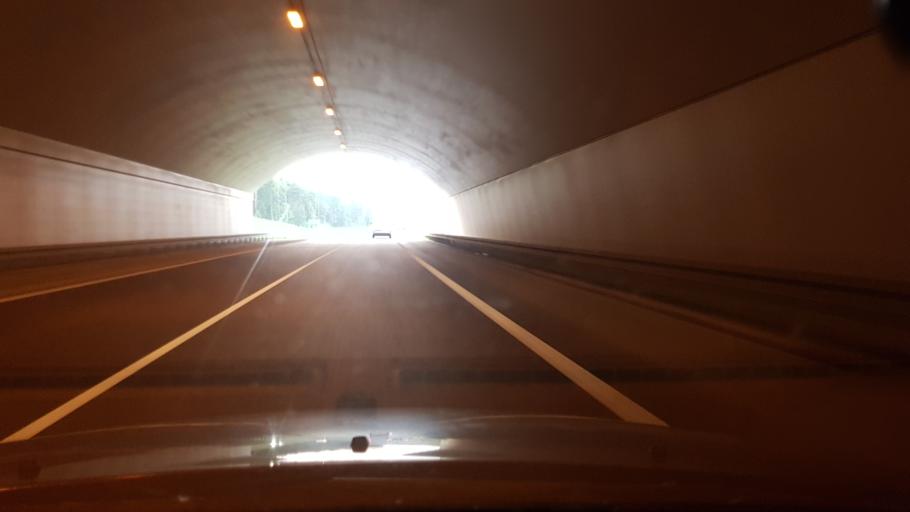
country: PL
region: Masovian Voivodeship
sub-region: Powiat mlawski
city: Wieczfnia Koscielna
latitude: 53.2523
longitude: 20.4243
